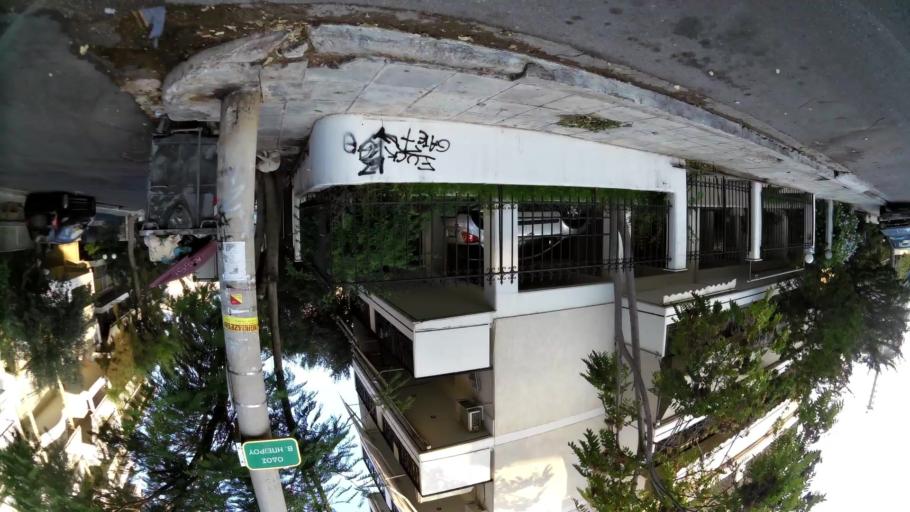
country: GR
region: Attica
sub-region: Nomarchia Athinas
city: Petroupolis
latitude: 38.0391
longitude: 23.6852
